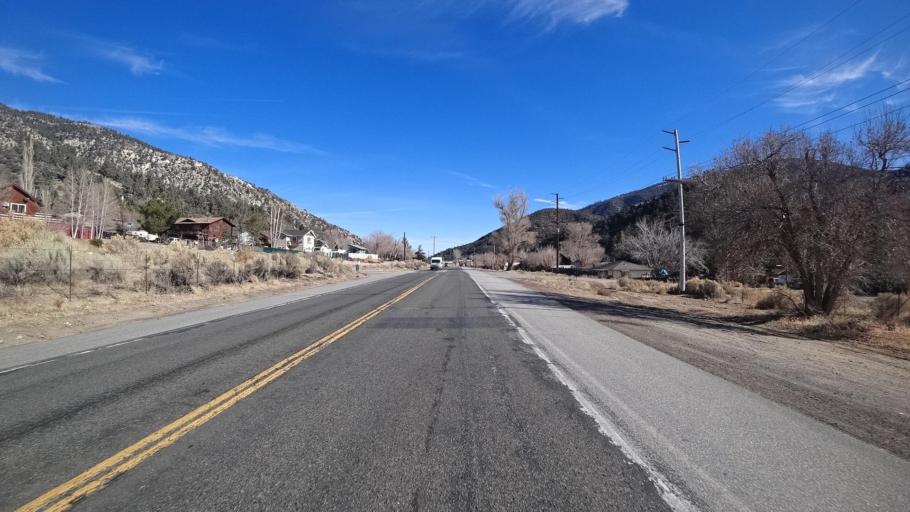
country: US
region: California
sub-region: Kern County
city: Frazier Park
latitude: 34.8186
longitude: -118.9968
